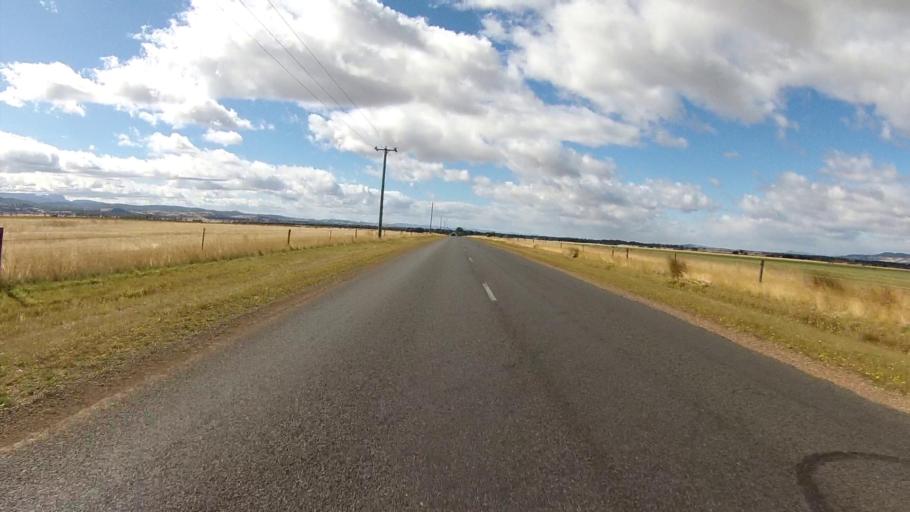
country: AU
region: Tasmania
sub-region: Northern Midlands
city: Evandale
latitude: -41.5901
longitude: 147.2640
